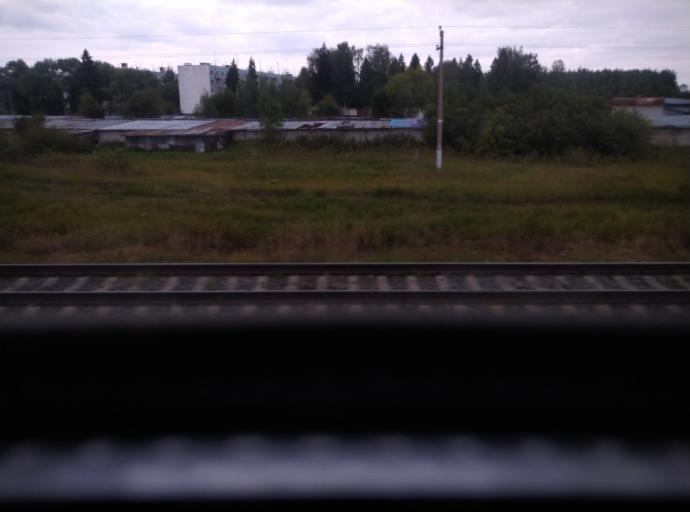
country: RU
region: Jaroslavl
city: Burmakino
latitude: 57.4369
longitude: 40.3150
